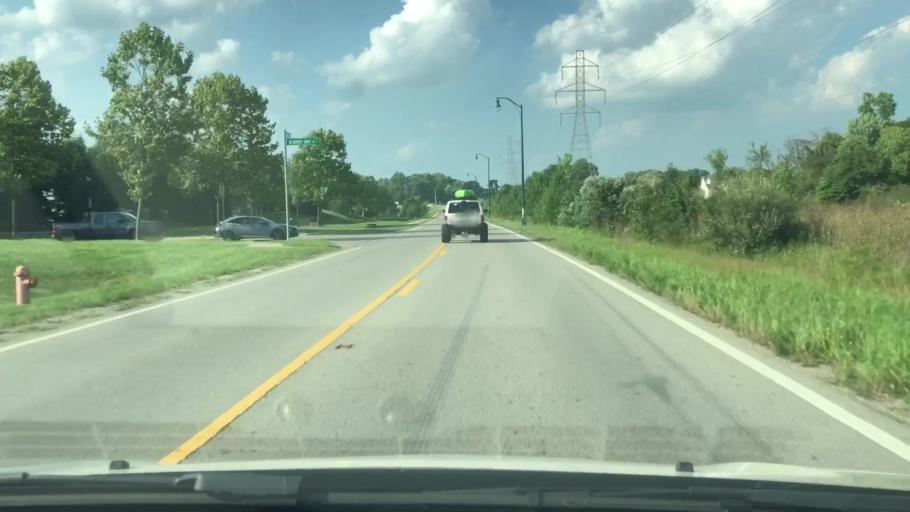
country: US
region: Ohio
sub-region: Franklin County
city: New Albany
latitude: 40.0950
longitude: -82.8487
